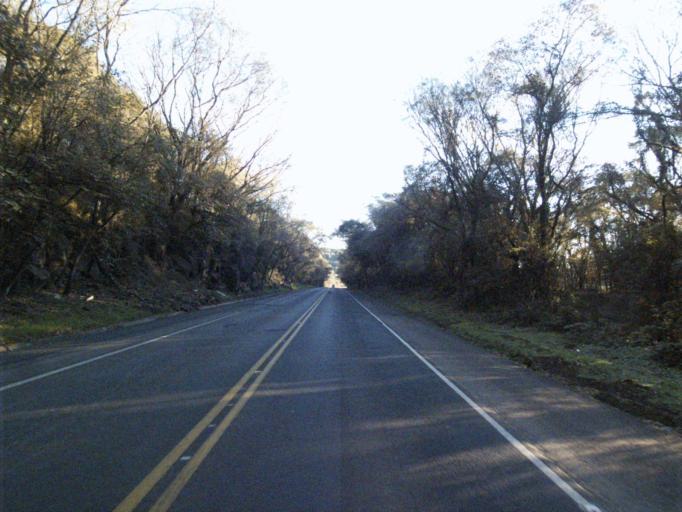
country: BR
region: Santa Catarina
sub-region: Chapeco
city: Chapeco
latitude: -26.8311
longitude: -53.0273
